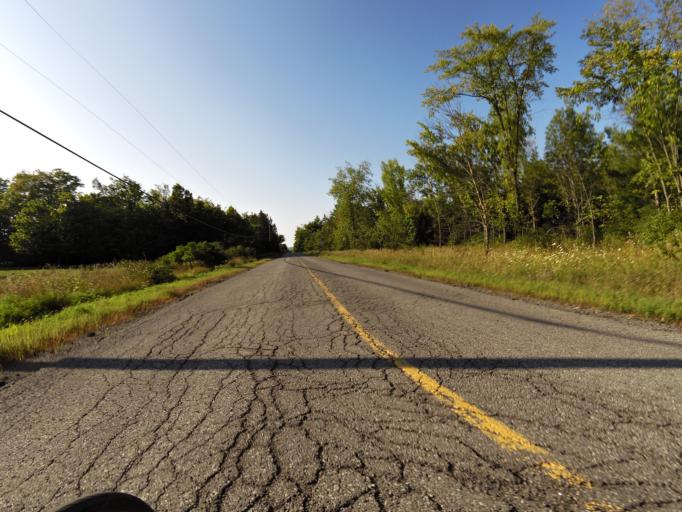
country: CA
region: Ontario
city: Bells Corners
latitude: 45.4778
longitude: -76.0411
